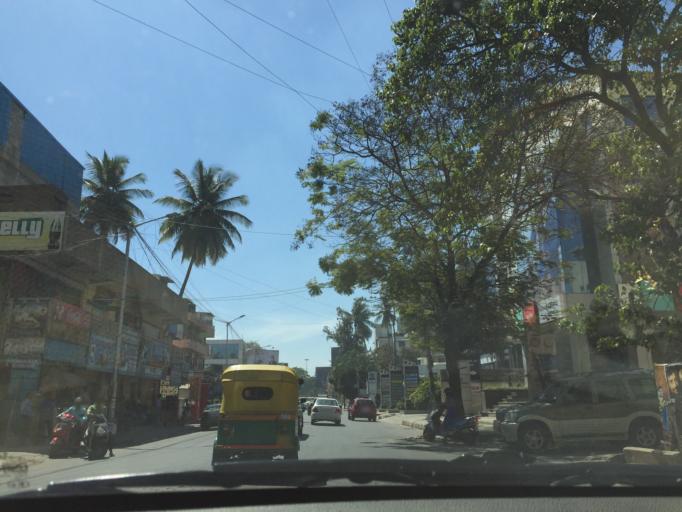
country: IN
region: Karnataka
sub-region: Bangalore Urban
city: Bangalore
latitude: 12.9581
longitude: 77.5863
